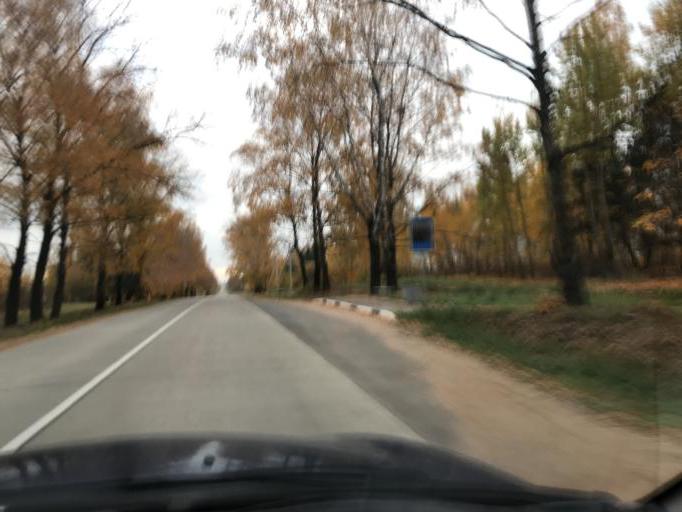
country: BY
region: Minsk
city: Machulishchy
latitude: 53.7671
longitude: 27.5977
